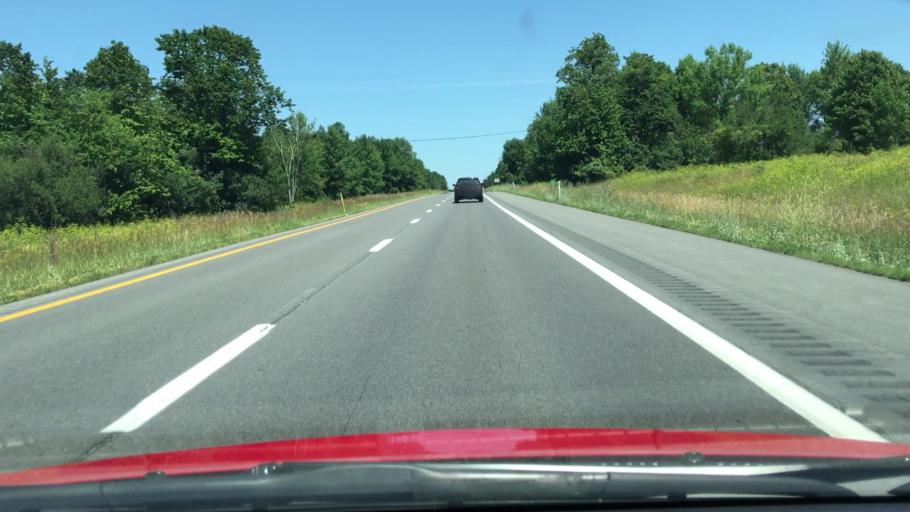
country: US
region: New York
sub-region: Clinton County
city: Cumberland Head
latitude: 44.7356
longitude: -73.4345
